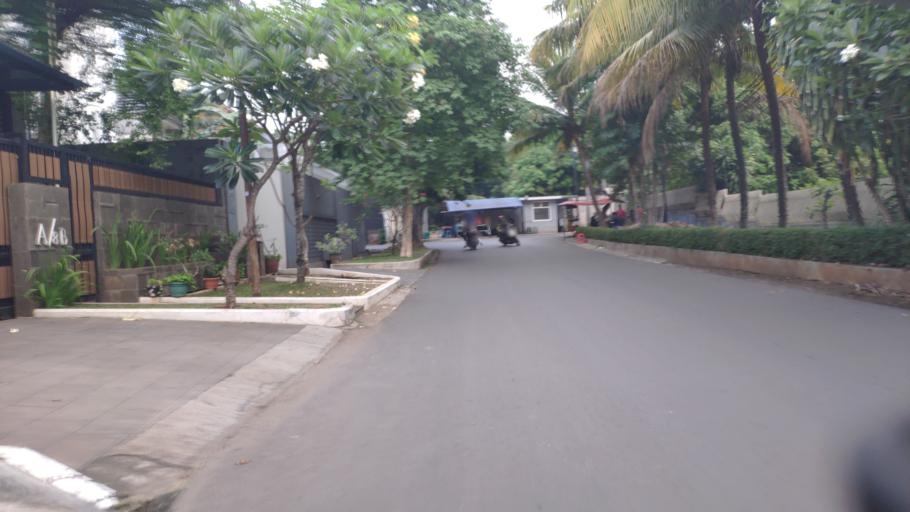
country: ID
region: West Java
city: Pamulang
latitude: -6.2985
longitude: 106.7998
